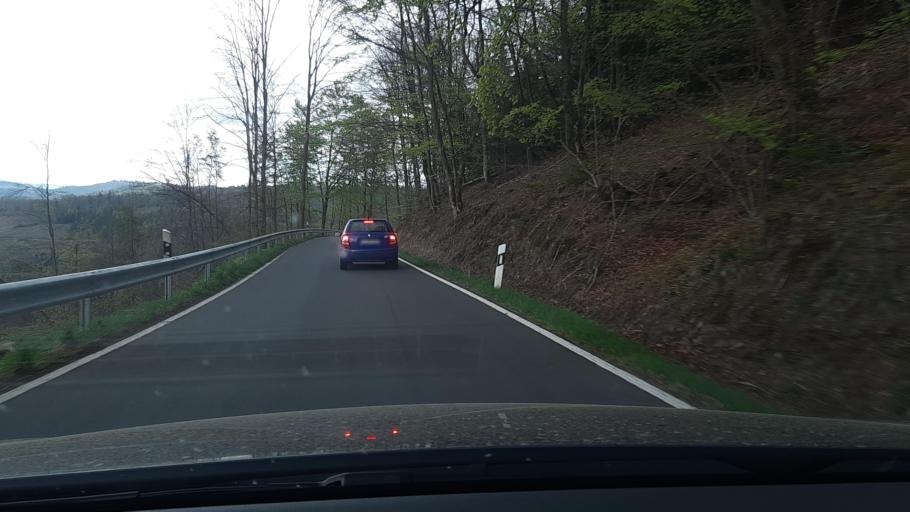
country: DE
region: North Rhine-Westphalia
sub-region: Regierungsbezirk Arnsberg
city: Bad Laasphe
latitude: 50.8890
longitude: 8.3857
